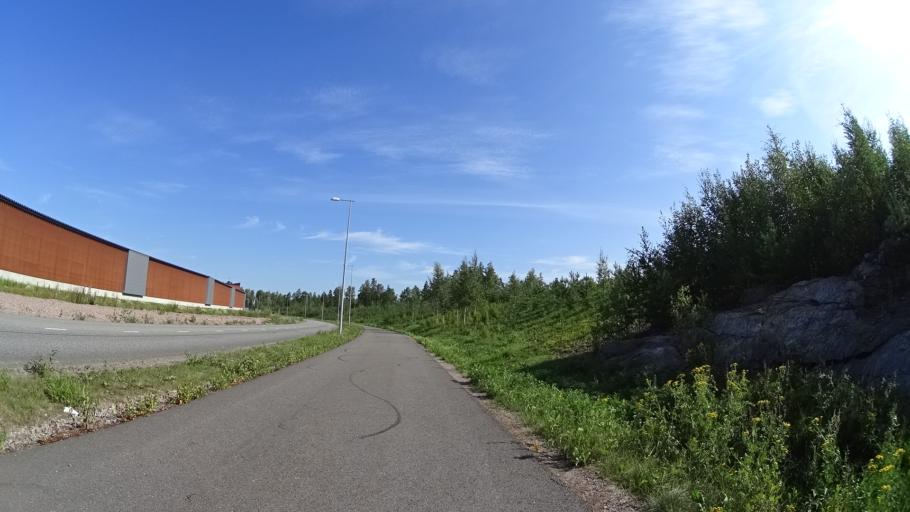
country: FI
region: Uusimaa
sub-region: Helsinki
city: Kilo
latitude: 60.2929
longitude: 24.7681
